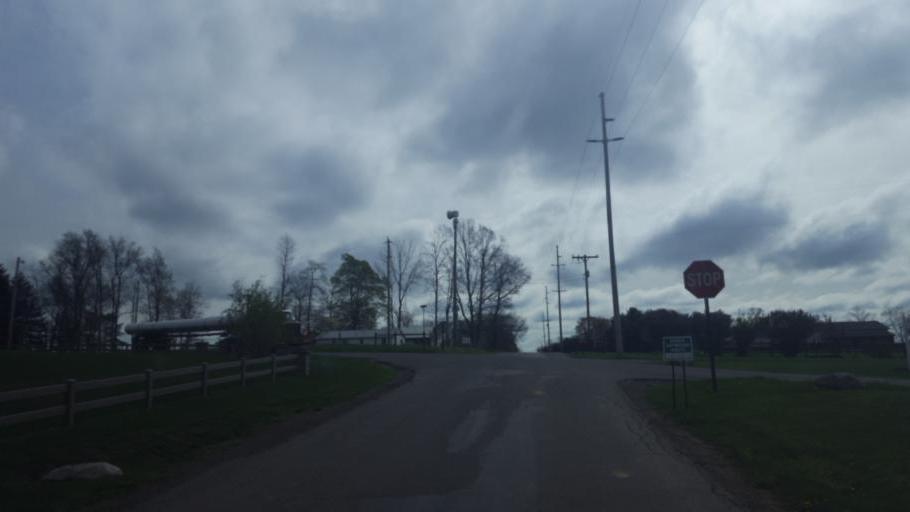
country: US
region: Ohio
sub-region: Wayne County
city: Apple Creek
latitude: 40.7117
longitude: -81.8321
